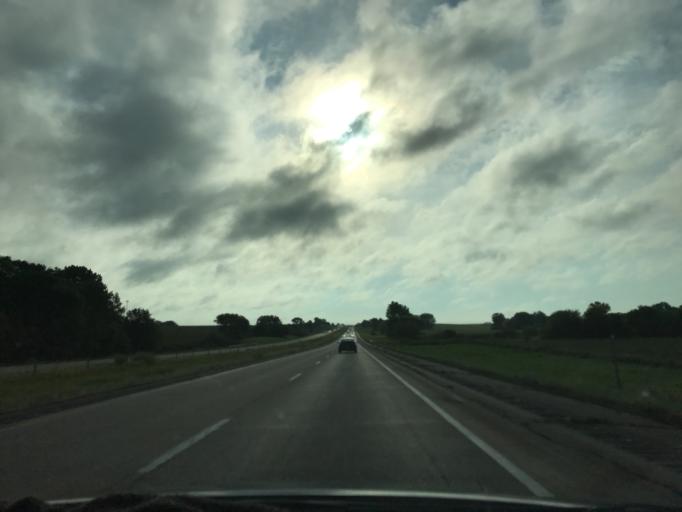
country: US
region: Iowa
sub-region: Cedar County
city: West Branch
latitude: 41.6673
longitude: -91.4130
